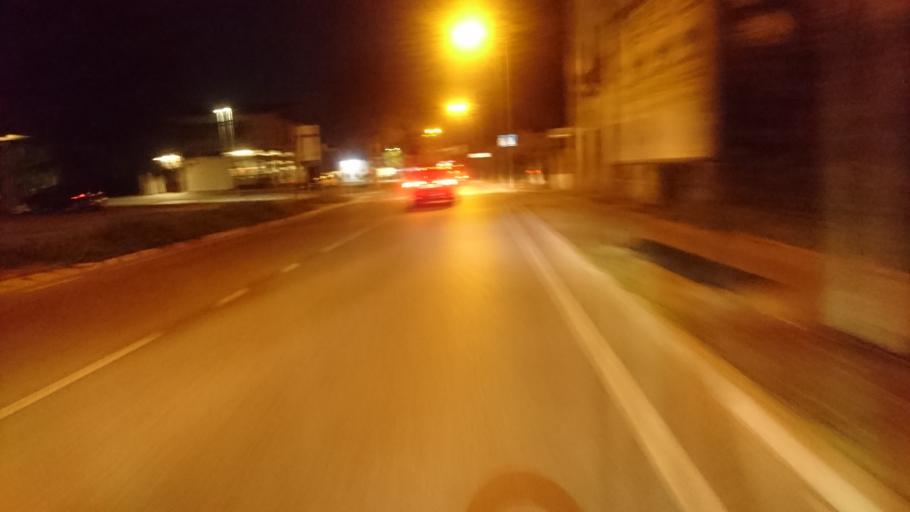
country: IT
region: Veneto
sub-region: Provincia di Padova
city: Abano Terme
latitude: 45.3625
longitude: 11.7943
